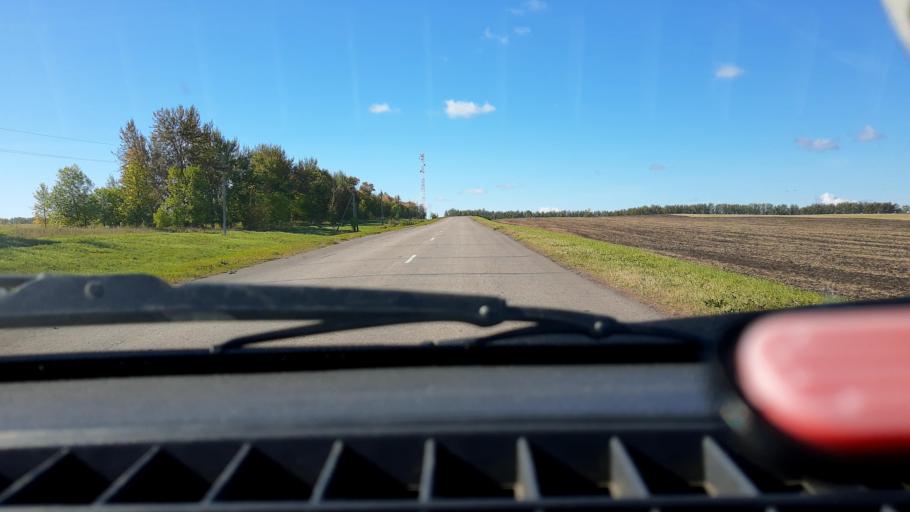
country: RU
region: Bashkortostan
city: Kushnarenkovo
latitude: 55.0791
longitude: 55.4675
